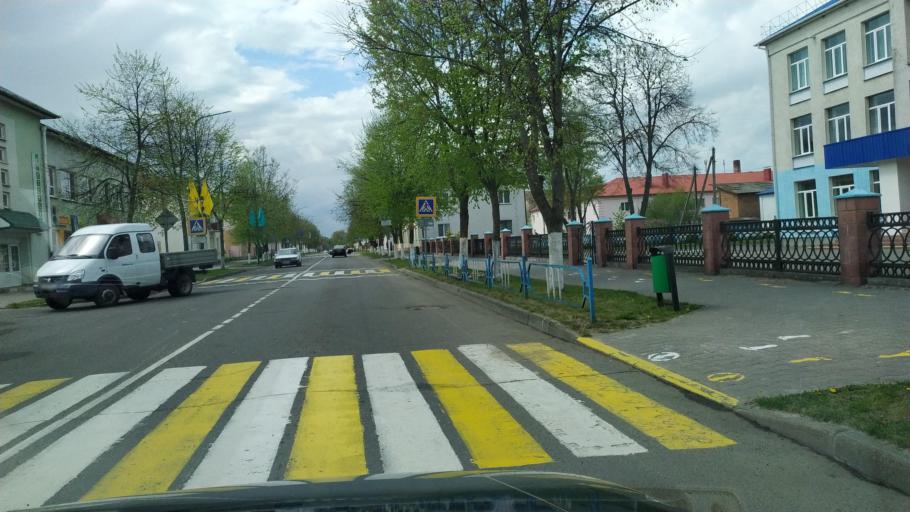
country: BY
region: Brest
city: Pruzhany
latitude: 52.5552
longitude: 24.4600
